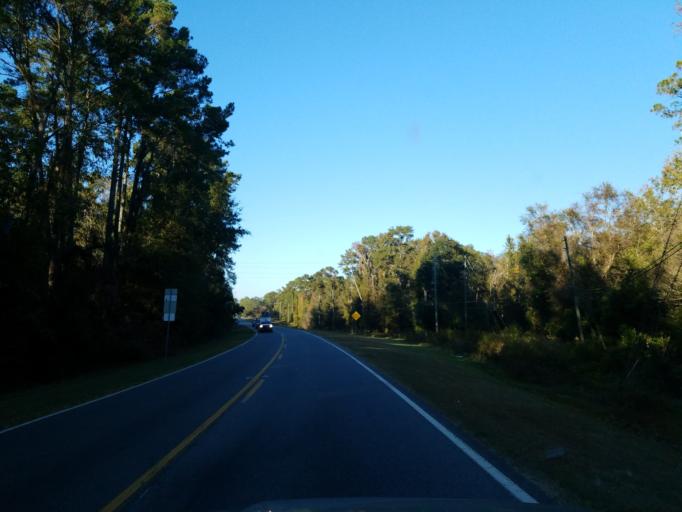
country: US
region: Georgia
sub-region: Lanier County
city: Lakeland
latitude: 31.0468
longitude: -83.0701
